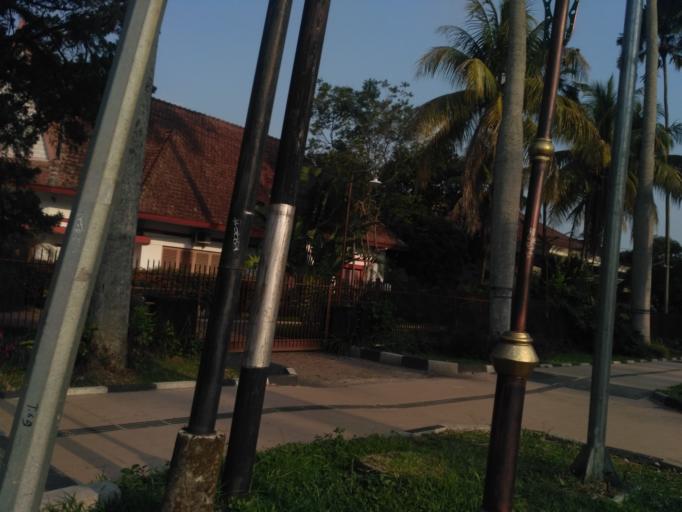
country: ID
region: East Java
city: Malang
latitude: -7.9689
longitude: 112.6236
